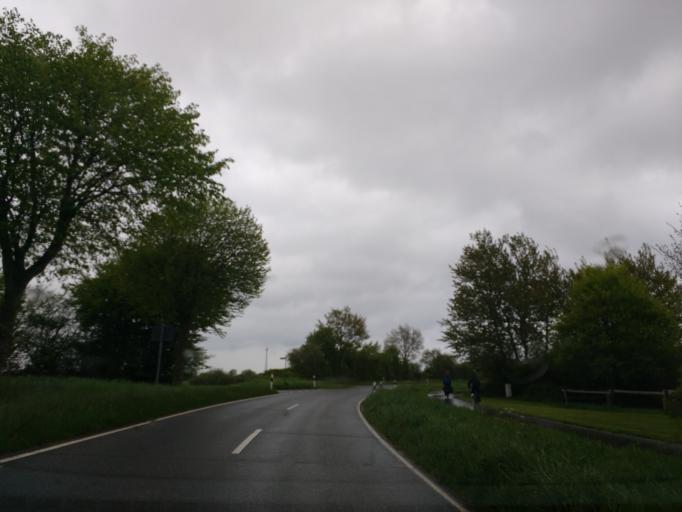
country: DE
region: Schleswig-Holstein
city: Waabs
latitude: 54.5345
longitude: 9.9817
